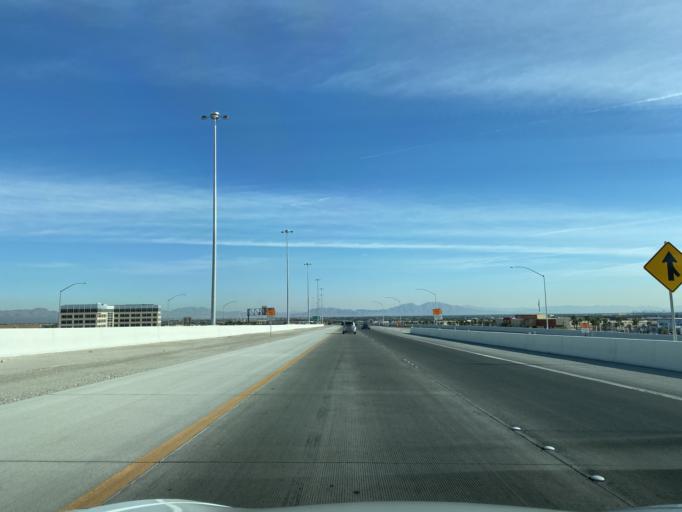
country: US
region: Nevada
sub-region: Clark County
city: Summerlin South
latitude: 36.2791
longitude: -115.2858
